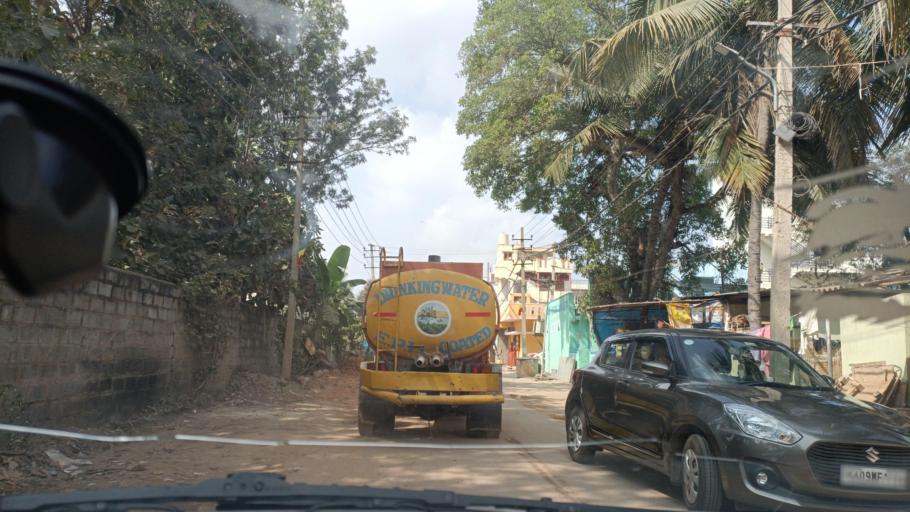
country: IN
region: Karnataka
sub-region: Bangalore Urban
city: Yelahanka
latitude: 13.1547
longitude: 77.6255
